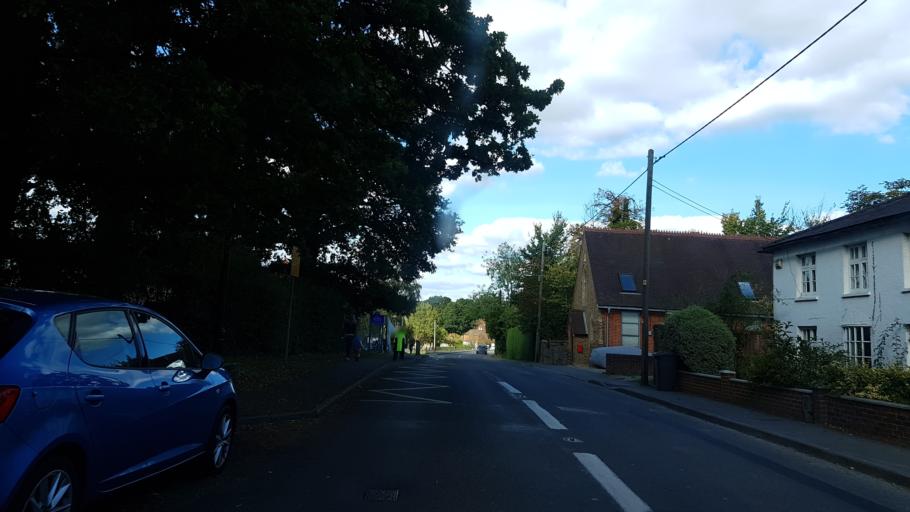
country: GB
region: England
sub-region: Surrey
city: Chiddingfold
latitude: 51.1124
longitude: -0.6278
